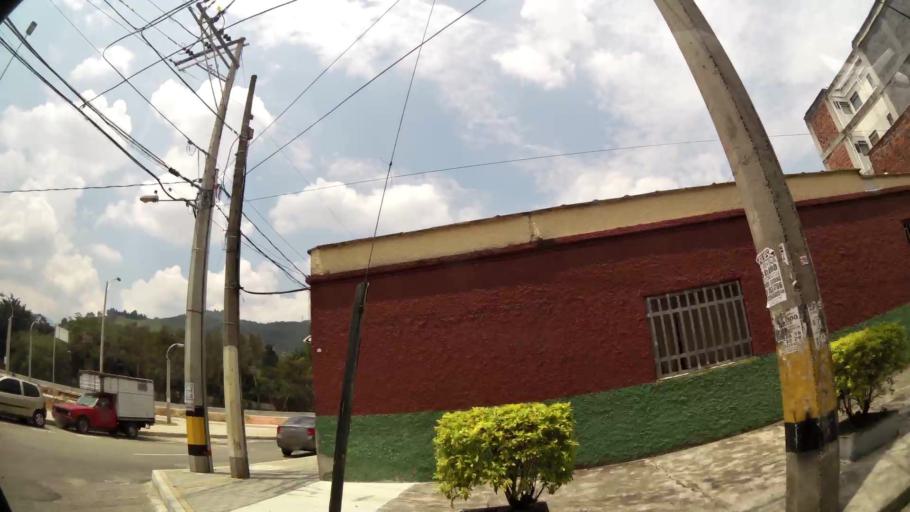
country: CO
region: Antioquia
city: Itagui
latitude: 6.1749
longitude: -75.6091
